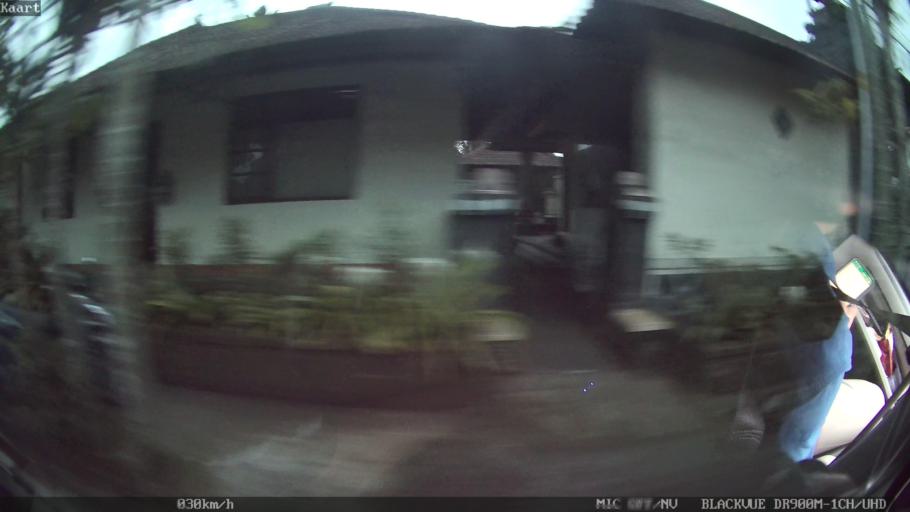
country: ID
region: Bali
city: Badung
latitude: -8.4270
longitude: 115.2462
